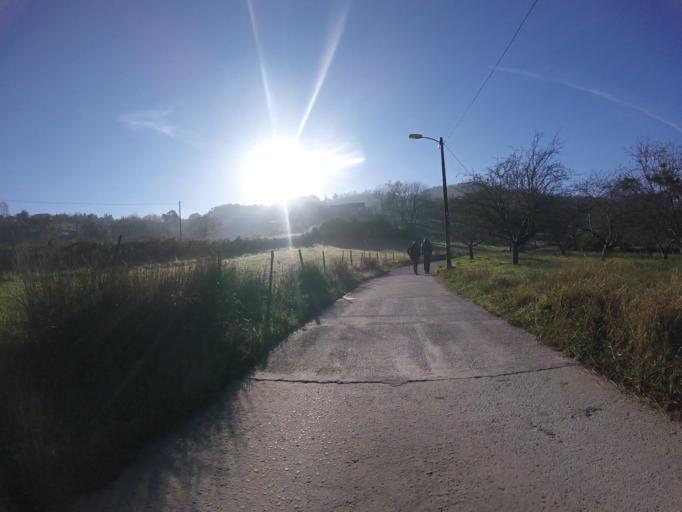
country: ES
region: Basque Country
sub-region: Provincia de Guipuzcoa
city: Lasarte
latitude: 43.2682
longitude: -2.0347
